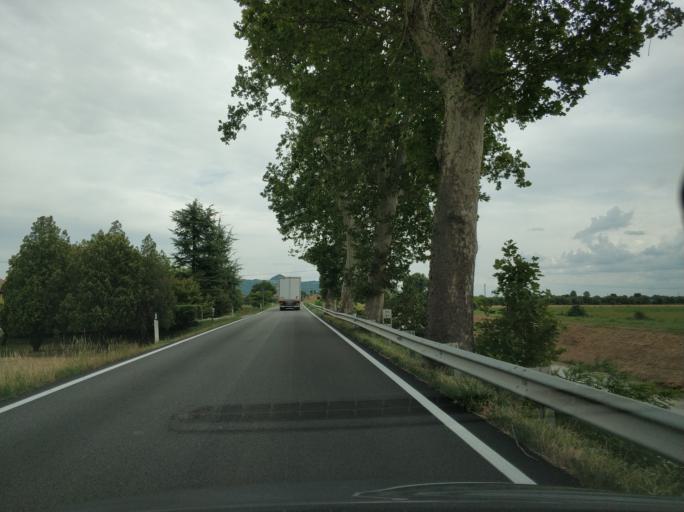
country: IT
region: Veneto
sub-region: Provincia di Padova
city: Lozzo Atestino
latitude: 45.2686
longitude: 11.5945
